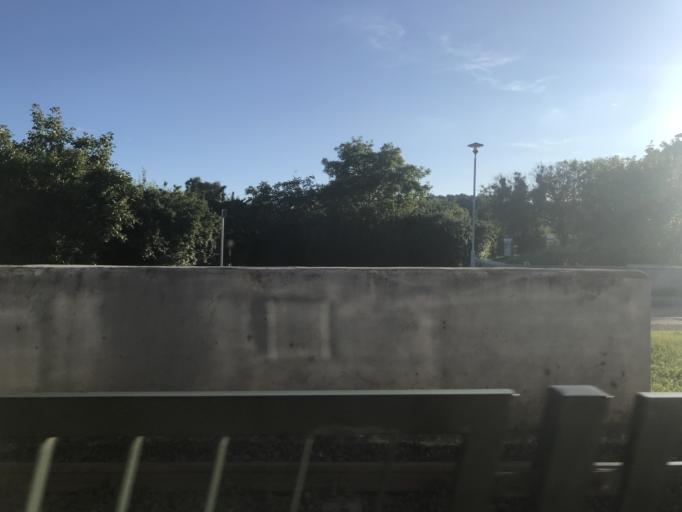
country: PL
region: Pomeranian Voivodeship
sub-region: Sopot
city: Sopot
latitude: 54.3959
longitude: 18.5716
